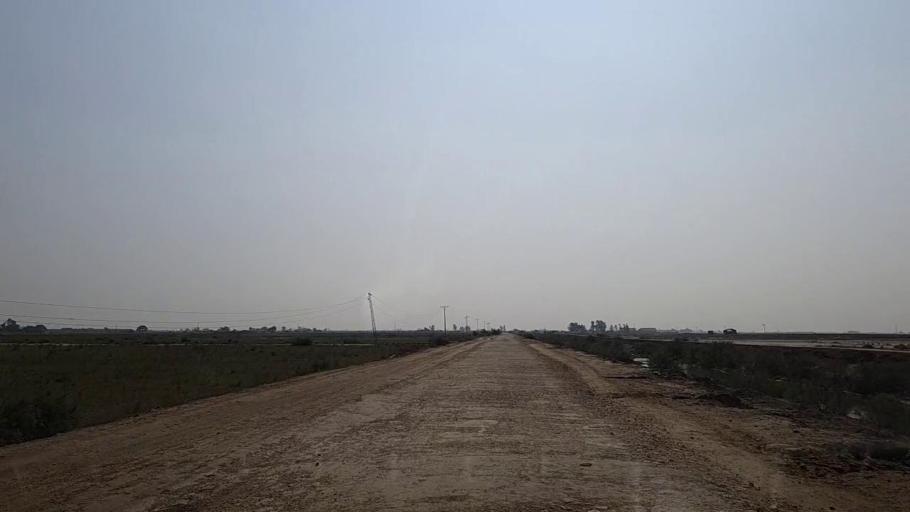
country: PK
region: Sindh
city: Thatta
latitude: 24.7168
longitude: 67.7684
